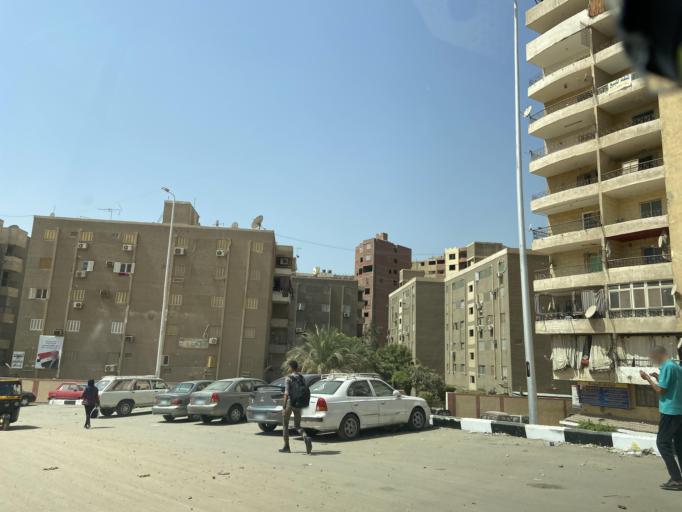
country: EG
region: Muhafazat al Qahirah
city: Cairo
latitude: 30.0626
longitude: 31.3796
